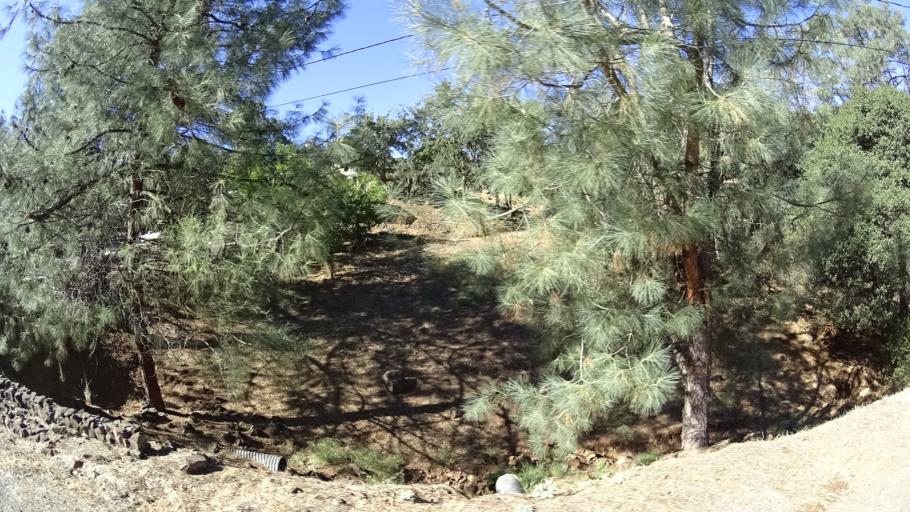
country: US
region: California
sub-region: Calaveras County
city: Rancho Calaveras
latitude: 38.1100
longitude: -120.8619
